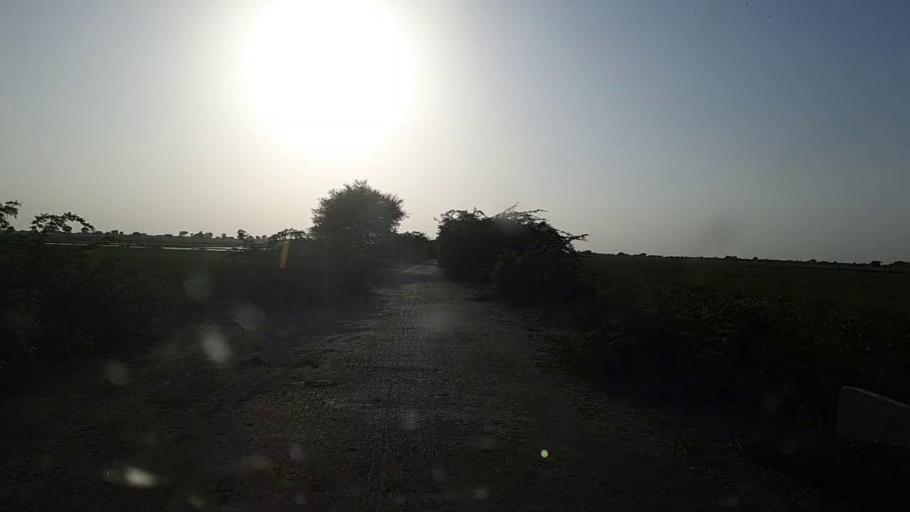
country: PK
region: Sindh
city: Mirpur Batoro
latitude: 24.5471
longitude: 68.4414
